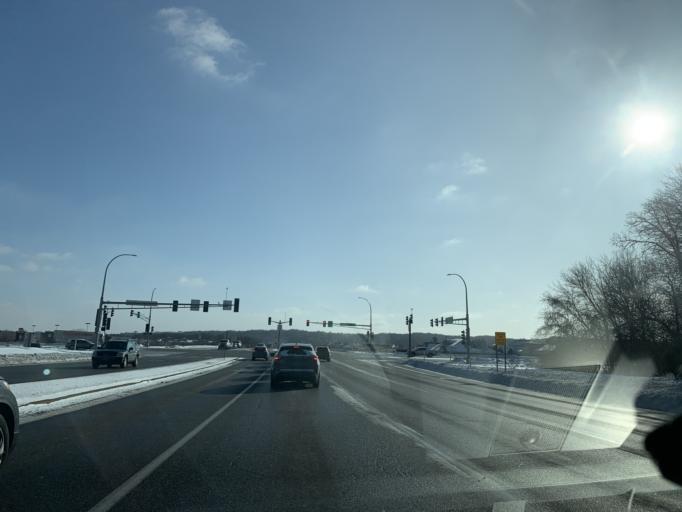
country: US
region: Minnesota
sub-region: Scott County
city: Prior Lake
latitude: 44.7746
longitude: -93.4161
